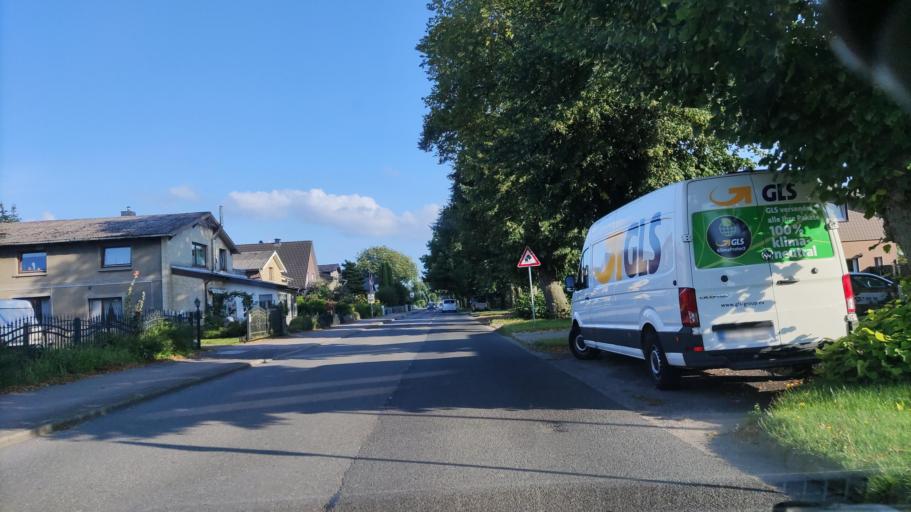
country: DE
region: Schleswig-Holstein
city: Brokstedt
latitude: 53.9876
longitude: 9.8266
